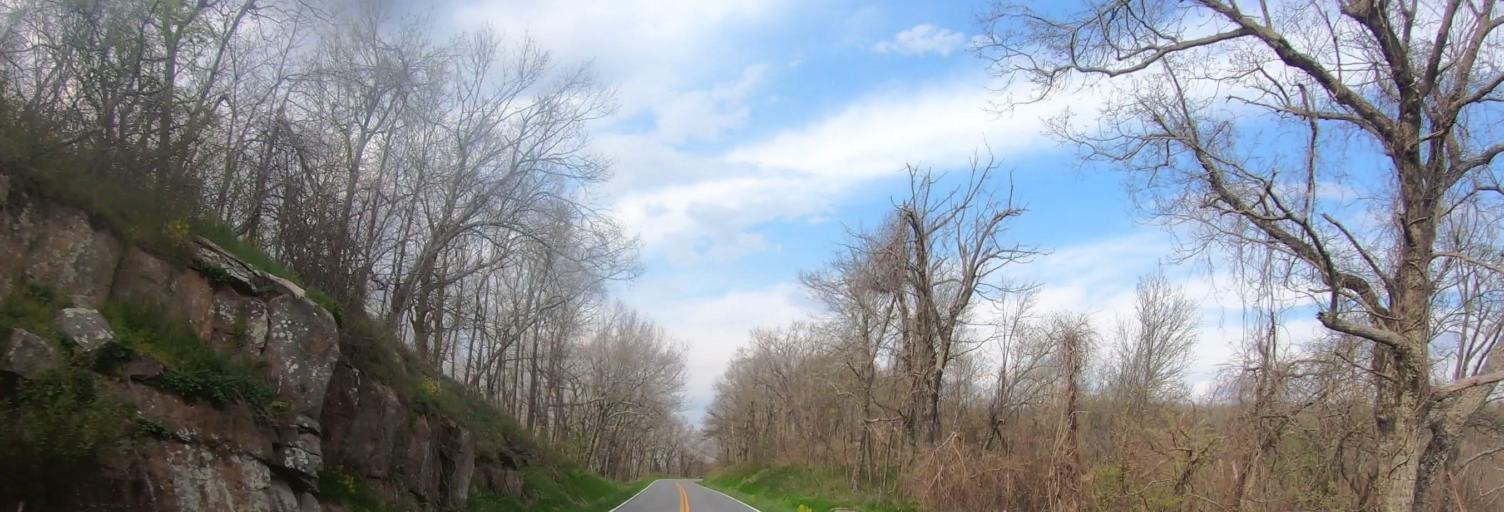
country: US
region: Virginia
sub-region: Rockingham County
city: Grottoes
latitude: 38.2509
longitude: -78.6870
